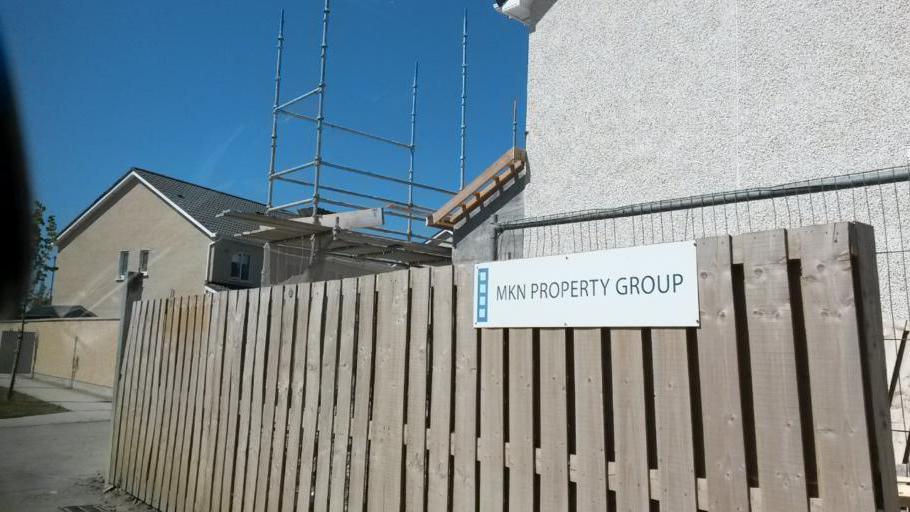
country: IE
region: Leinster
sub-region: Fingal County
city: Swords
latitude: 53.4490
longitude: -6.2518
